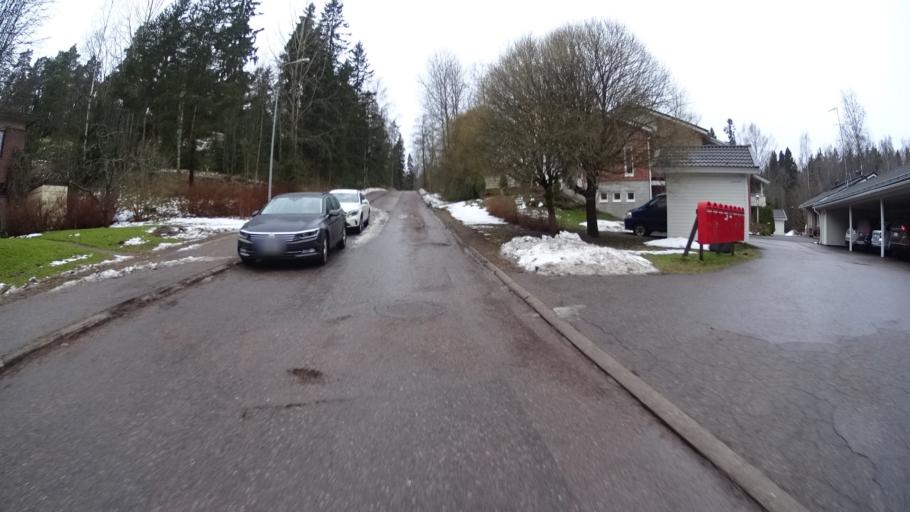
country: FI
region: Uusimaa
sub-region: Helsinki
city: Koukkuniemi
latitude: 60.1850
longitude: 24.7574
